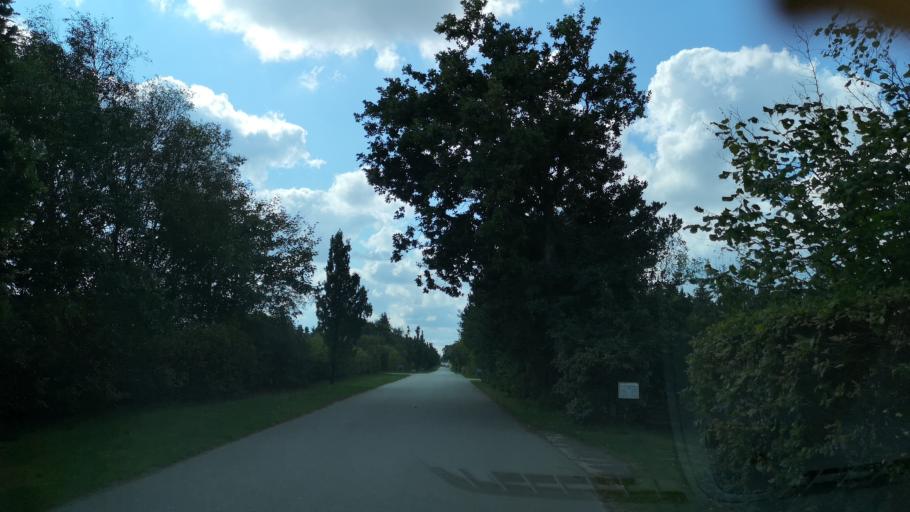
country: DK
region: Central Jutland
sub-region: Ringkobing-Skjern Kommune
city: Skjern
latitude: 55.8908
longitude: 8.3608
